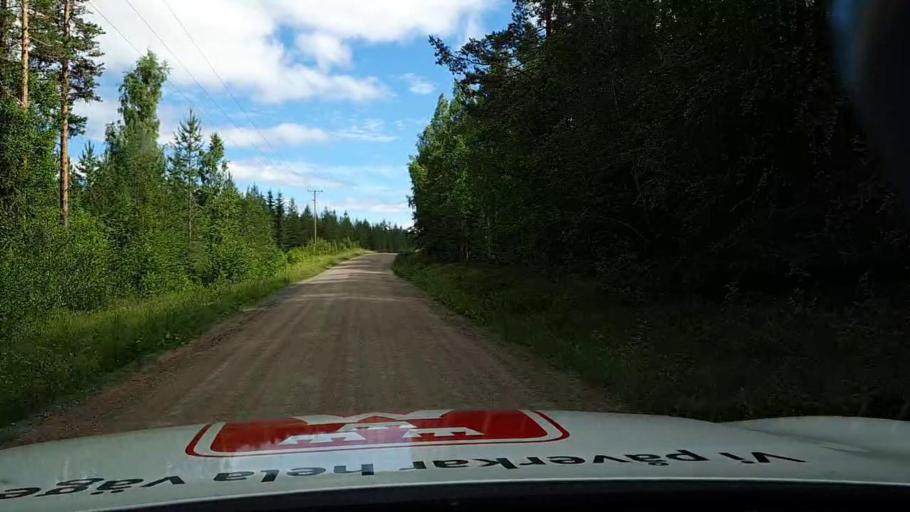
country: SE
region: Vaesternorrland
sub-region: Ange Kommun
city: Fransta
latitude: 62.7777
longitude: 16.1668
